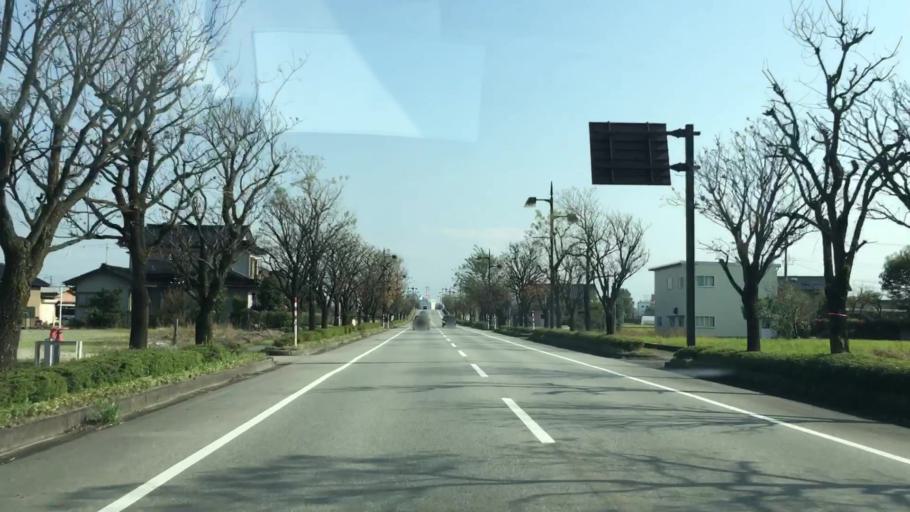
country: JP
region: Toyama
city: Toyama-shi
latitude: 36.6432
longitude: 137.2001
